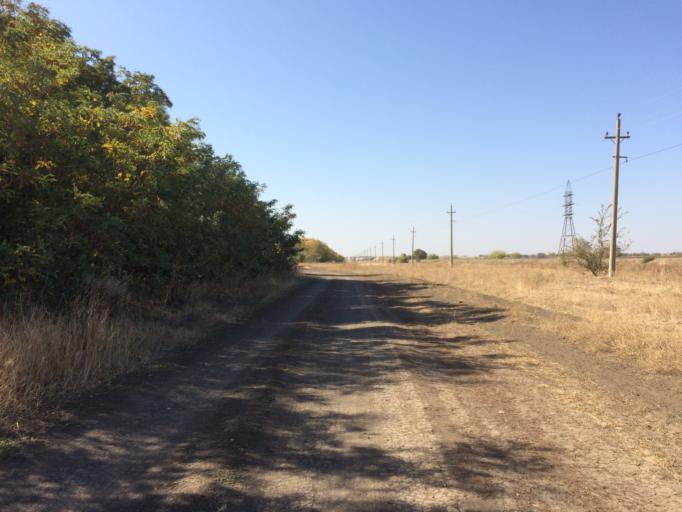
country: RU
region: Rostov
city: Tselina
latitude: 46.5283
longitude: 41.1847
